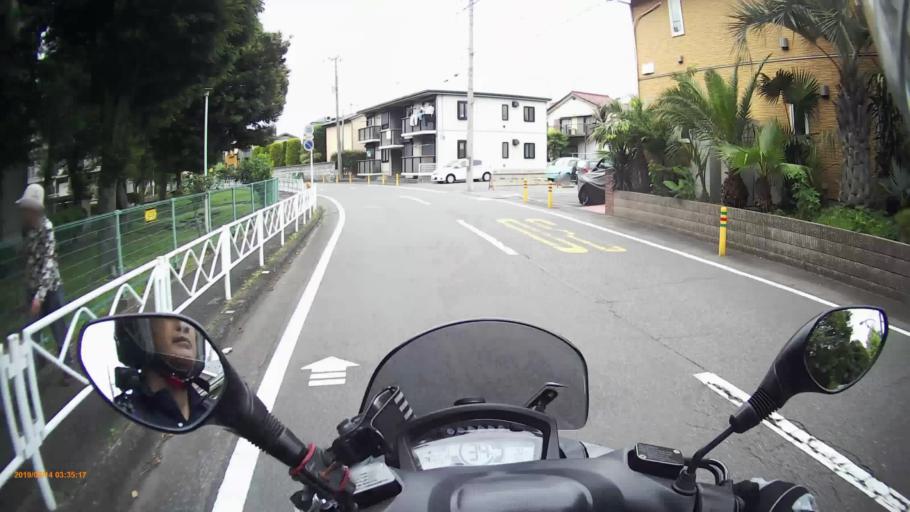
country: JP
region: Kanagawa
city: Minami-rinkan
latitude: 35.4142
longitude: 139.4496
